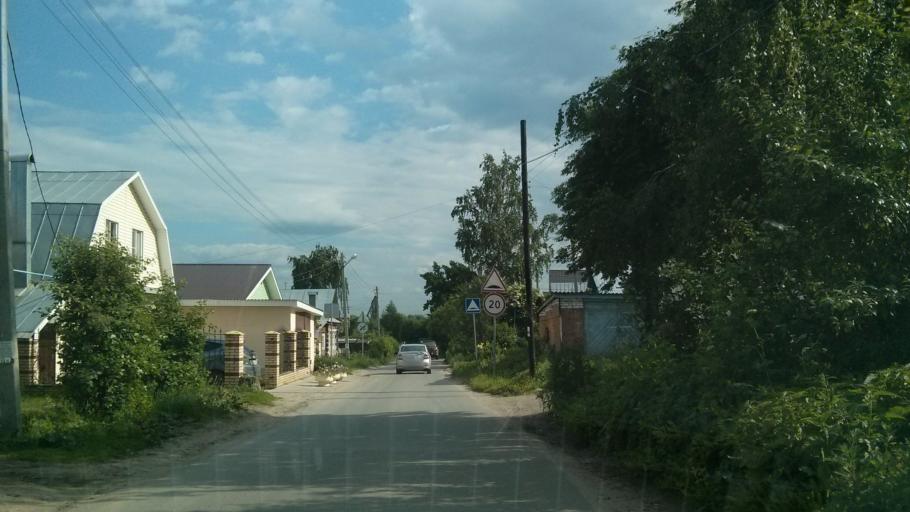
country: RU
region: Nizjnij Novgorod
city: Afonino
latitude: 56.2847
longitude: 44.1006
